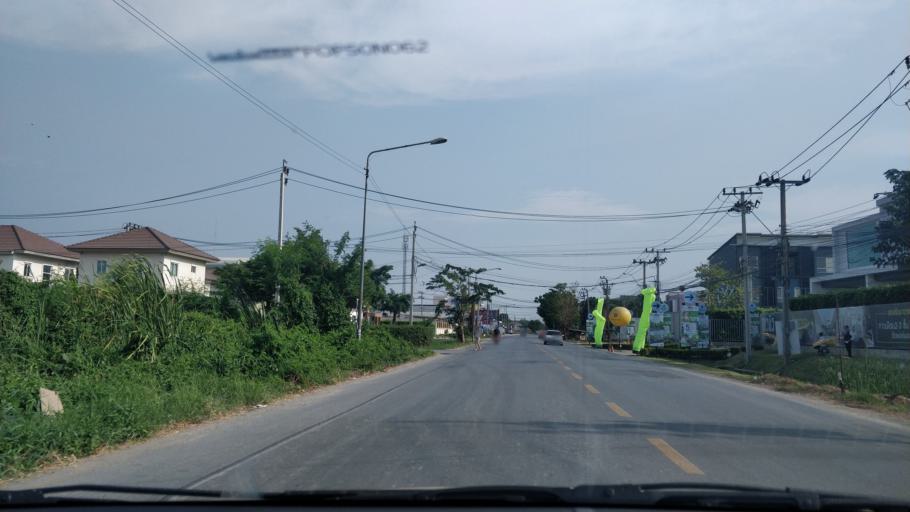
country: TH
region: Bangkok
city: Saphan Sung
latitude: 13.7424
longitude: 100.7164
